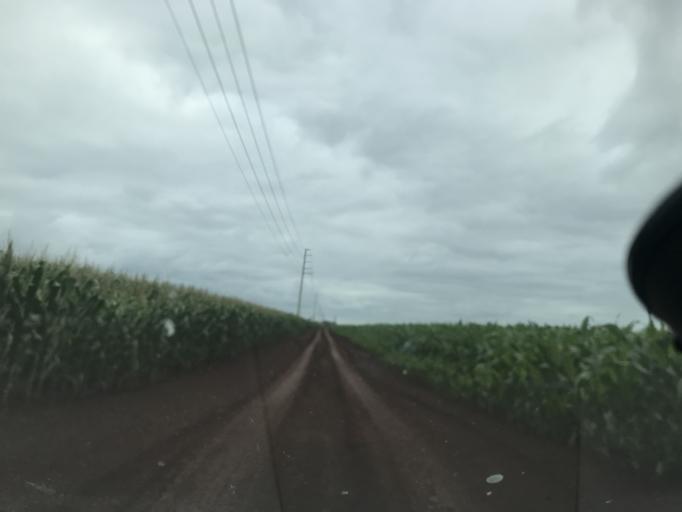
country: BR
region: Parana
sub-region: Palotina
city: Palotina
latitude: -24.3032
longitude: -53.8204
